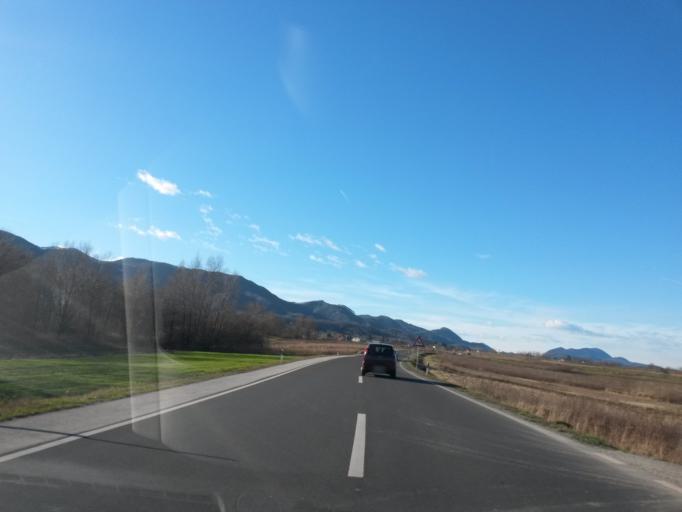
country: HR
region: Varazdinska
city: Ivanec
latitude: 46.2265
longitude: 16.1052
